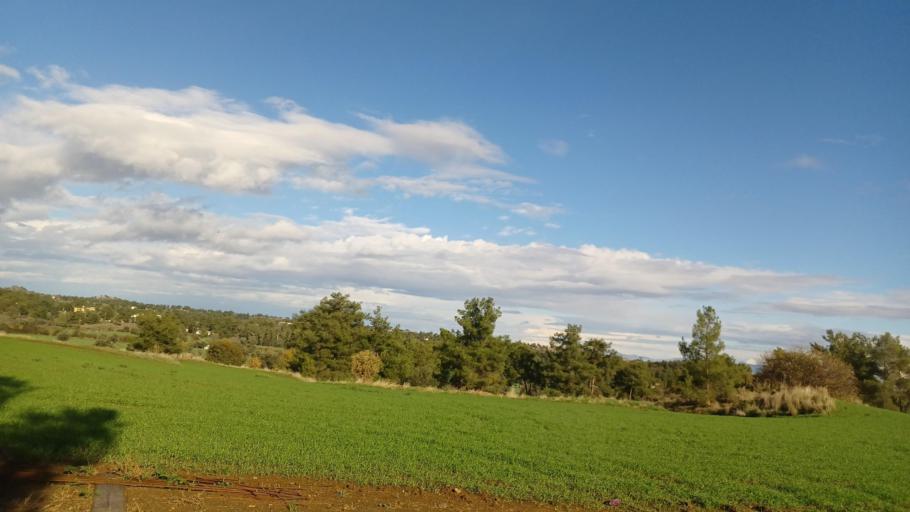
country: CY
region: Lefkosia
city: Lythrodontas
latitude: 34.9527
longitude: 33.3087
